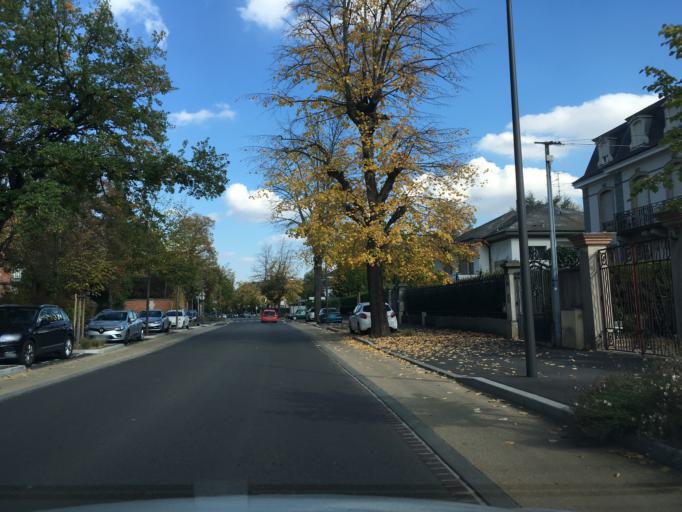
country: FR
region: Alsace
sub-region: Departement du Haut-Rhin
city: Colmar
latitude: 48.0680
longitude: 7.3485
